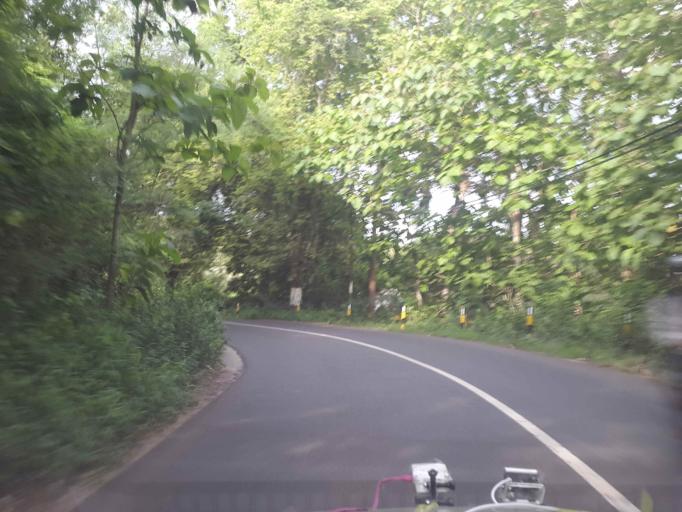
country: ID
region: East Java
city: Senmasen
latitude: -6.9883
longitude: 113.8633
